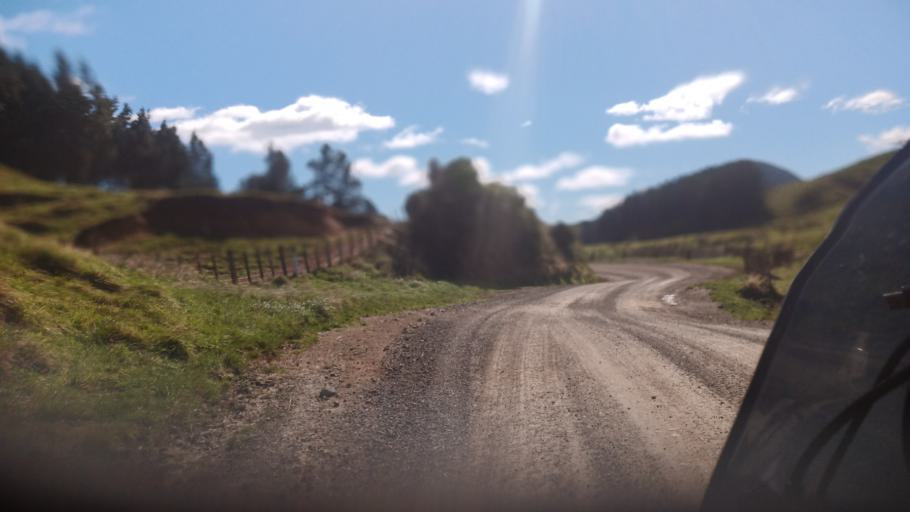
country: NZ
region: Bay of Plenty
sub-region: Opotiki District
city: Opotiki
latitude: -38.3357
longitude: 177.5787
